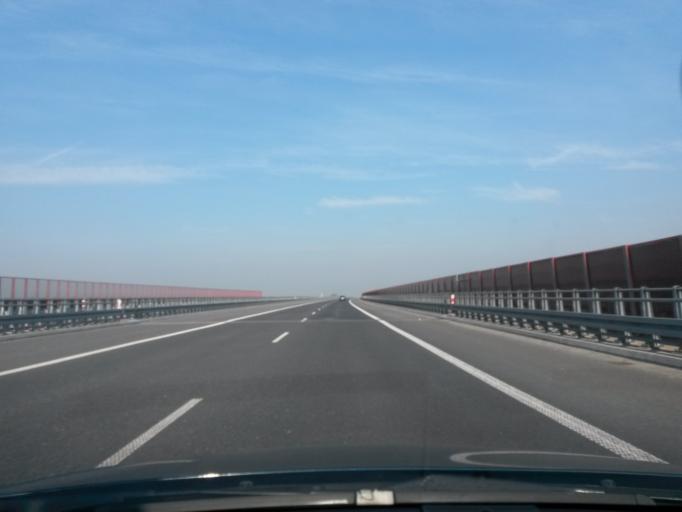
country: PL
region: Lodz Voivodeship
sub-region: Powiat leczycki
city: Piatek
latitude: 52.1308
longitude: 19.4902
